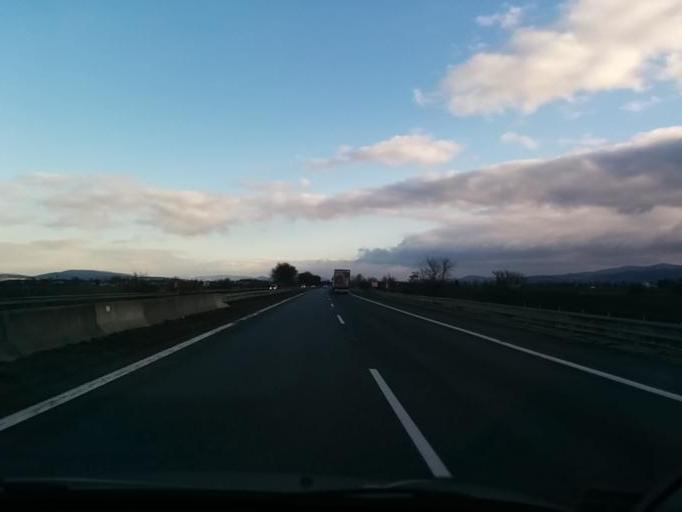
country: SK
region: Trnavsky
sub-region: Okres Trnava
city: Piestany
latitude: 48.6040
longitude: 17.7940
